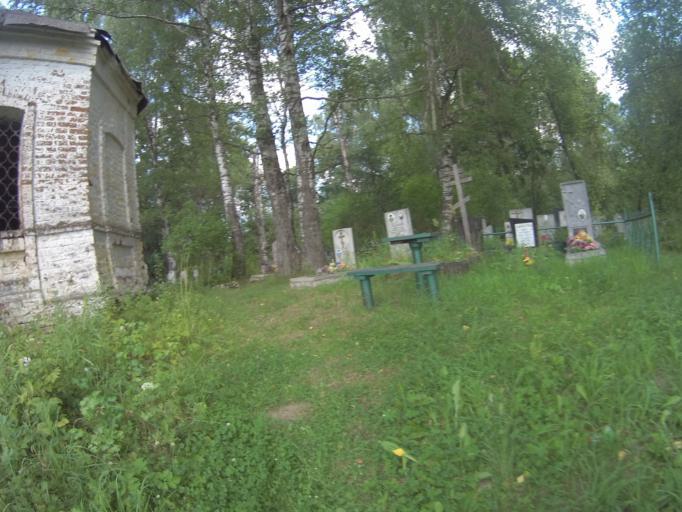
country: RU
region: Vladimir
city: Imeni Vorovskogo
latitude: 55.7388
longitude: 40.9552
